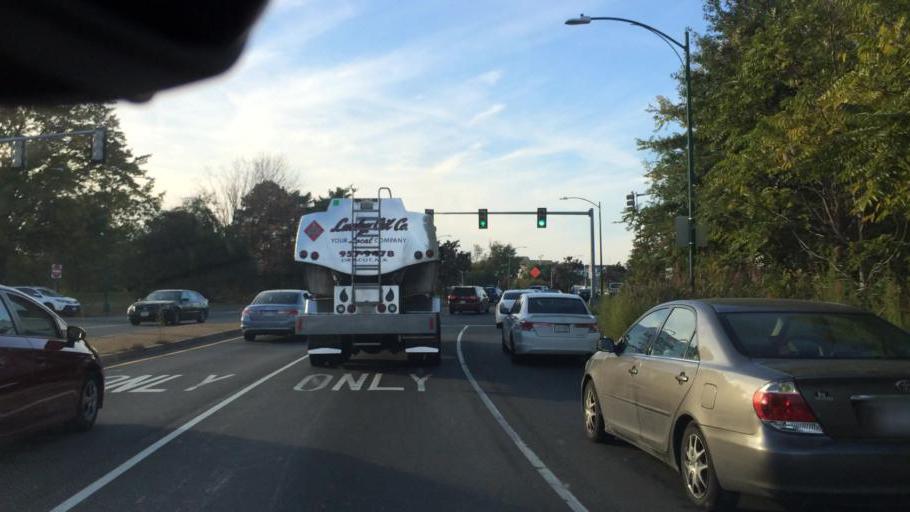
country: US
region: Massachusetts
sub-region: Middlesex County
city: Everett
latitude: 42.4018
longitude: -71.0678
